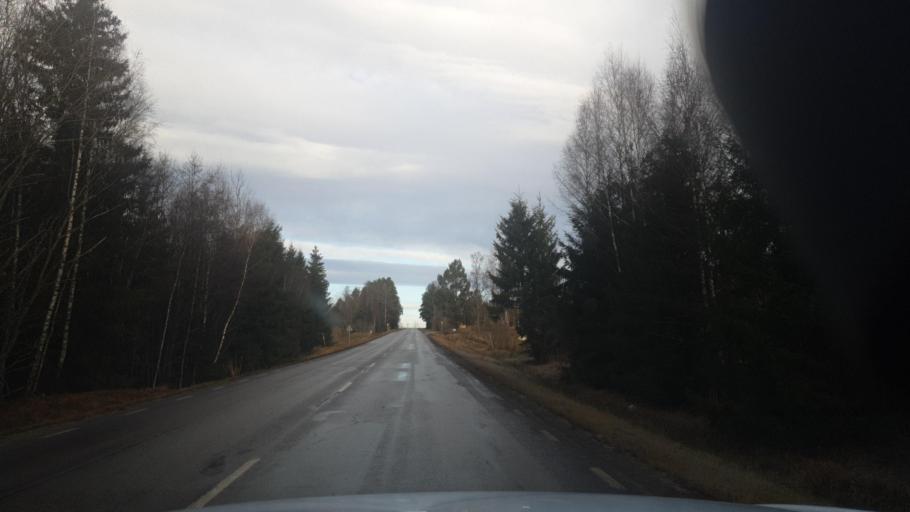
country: SE
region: Vaermland
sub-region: Arvika Kommun
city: Arvika
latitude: 59.6853
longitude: 12.6321
